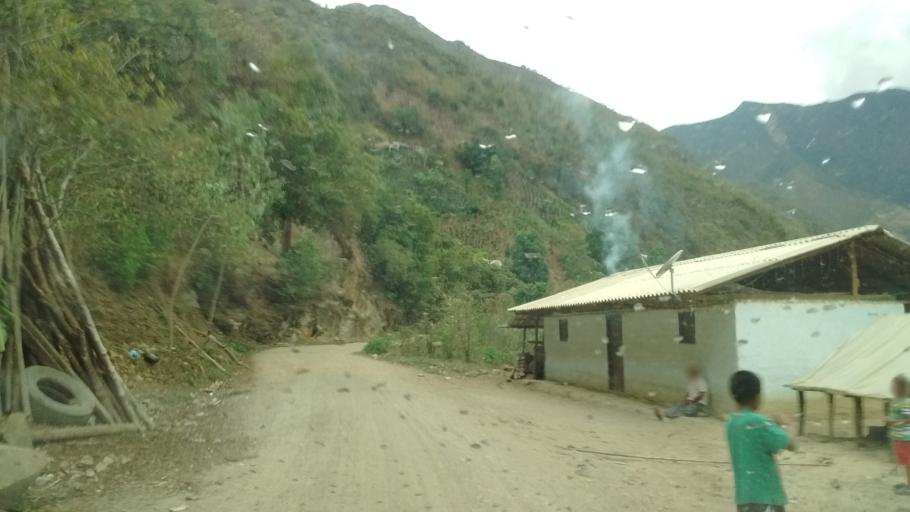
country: CO
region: Cauca
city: La Vega
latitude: 2.0411
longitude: -76.7973
